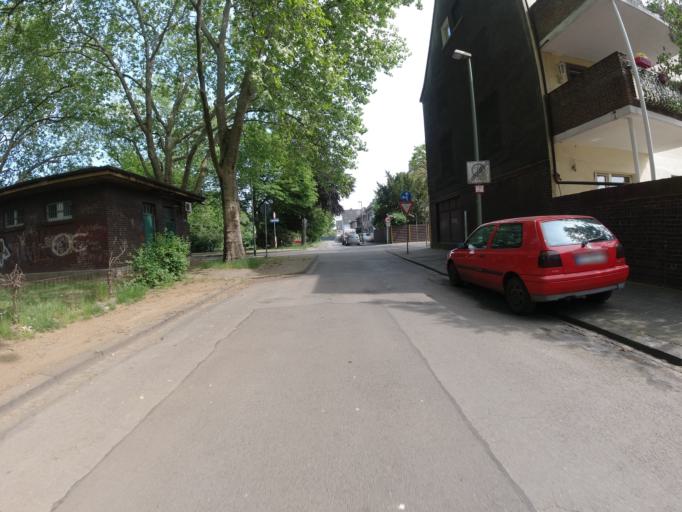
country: DE
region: North Rhine-Westphalia
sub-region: Regierungsbezirk Dusseldorf
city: Hochfeld
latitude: 51.3917
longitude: 6.7104
